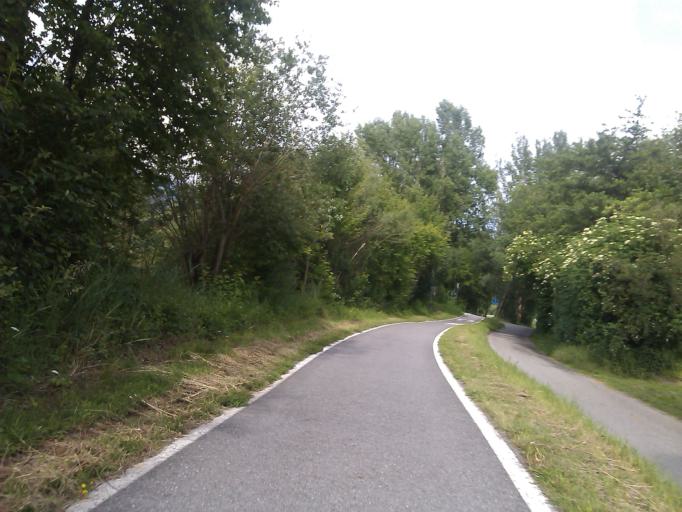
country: IT
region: Trentino-Alto Adige
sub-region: Bolzano
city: Lasa
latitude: 46.6206
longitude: 10.6614
